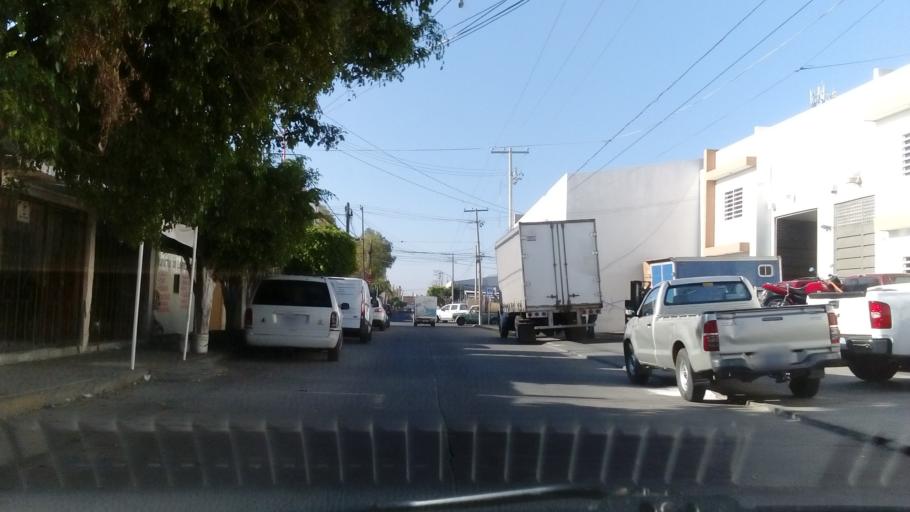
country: MX
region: Guanajuato
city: Leon
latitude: 21.1150
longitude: -101.7084
